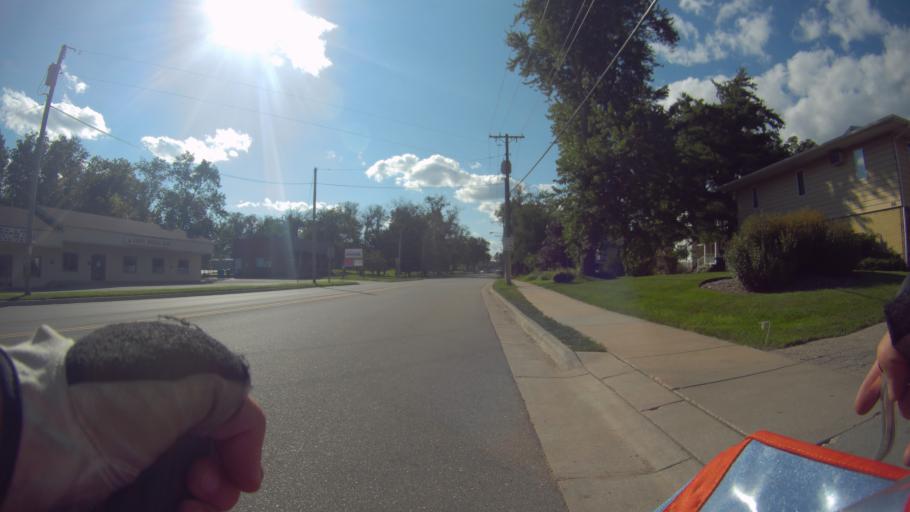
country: US
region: Wisconsin
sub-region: Dane County
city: Oregon
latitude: 42.9186
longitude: -89.3745
